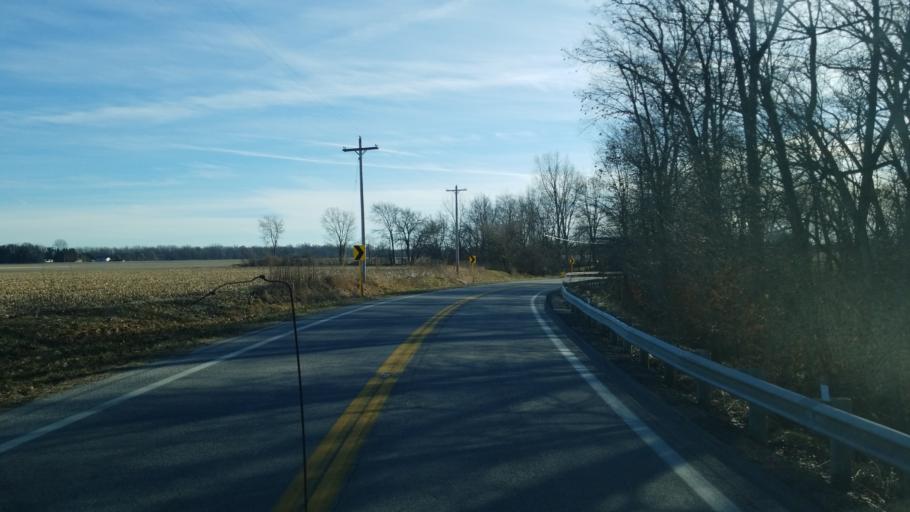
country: US
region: Ohio
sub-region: Sandusky County
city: Green Springs
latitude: 41.2942
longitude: -83.0511
